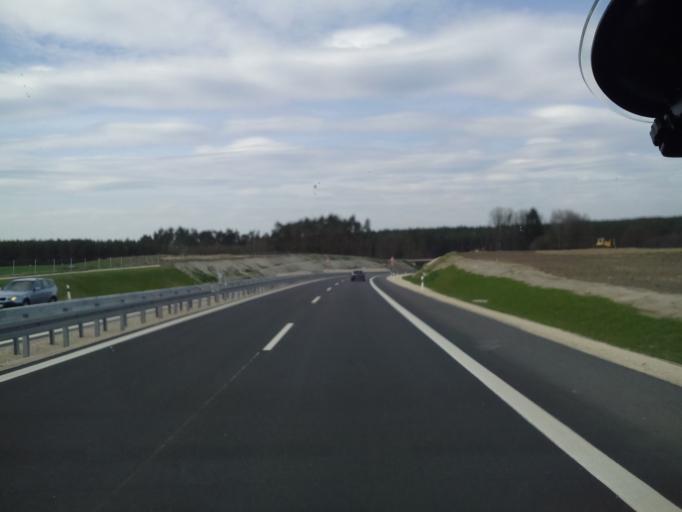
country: DE
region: Bavaria
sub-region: Regierungsbezirk Mittelfranken
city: Roth
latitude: 49.2053
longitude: 11.0750
